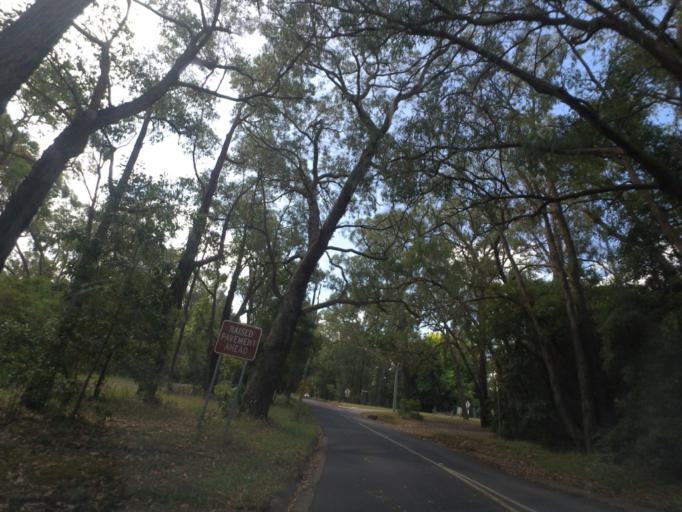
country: AU
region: Victoria
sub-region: Yarra Ranges
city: Montrose
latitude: -37.7895
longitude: 145.3537
